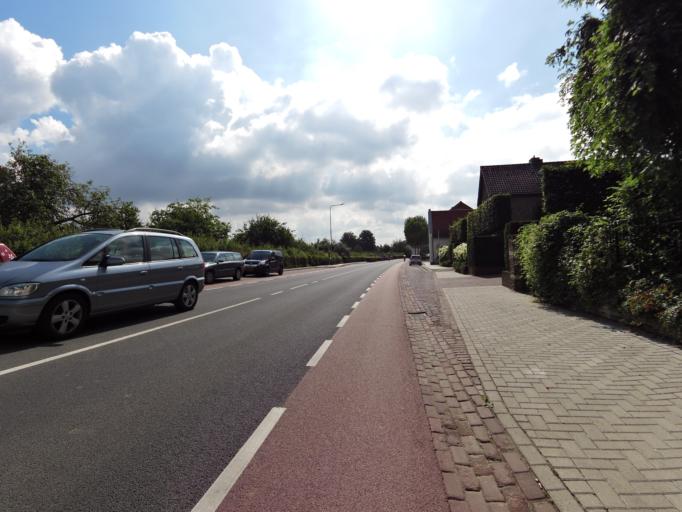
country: NL
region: Limburg
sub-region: Valkenburg aan de Geul
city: Schin op Geul
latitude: 50.8544
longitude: 5.8552
